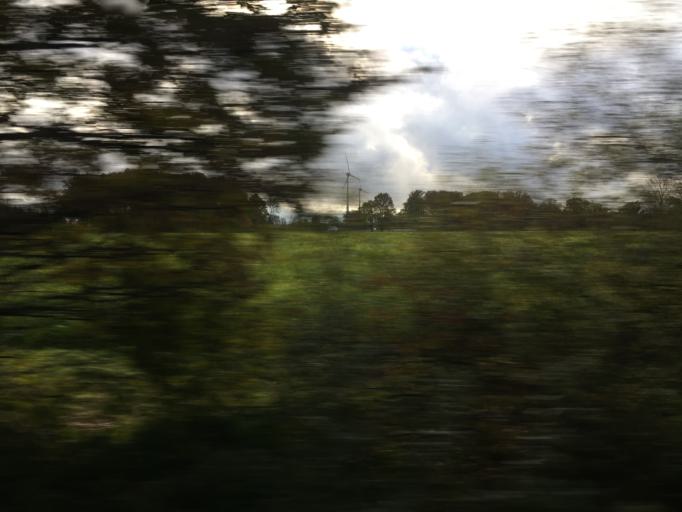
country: DE
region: North Rhine-Westphalia
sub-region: Regierungsbezirk Munster
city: Steinfurt
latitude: 52.1268
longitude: 7.3584
